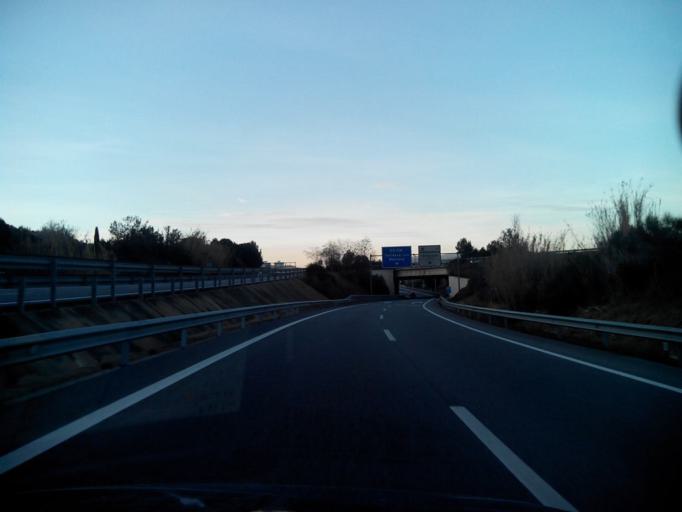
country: ES
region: Catalonia
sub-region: Provincia de Barcelona
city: Terrassa
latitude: 41.5418
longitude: 2.0160
